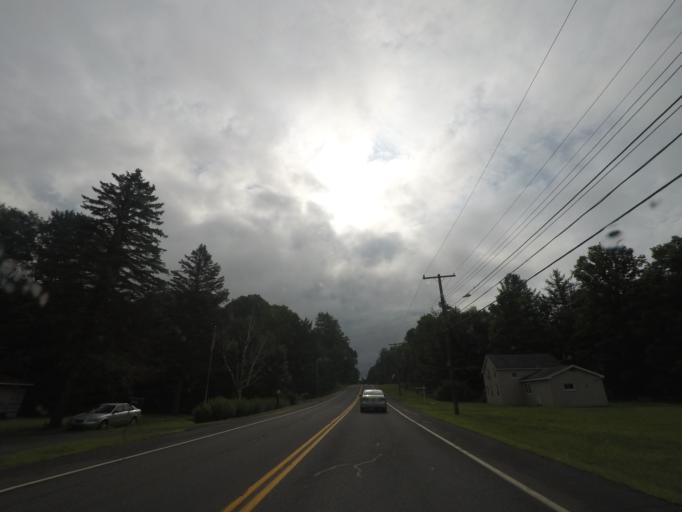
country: US
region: New York
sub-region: Rensselaer County
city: Nassau
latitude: 42.4966
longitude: -73.5242
